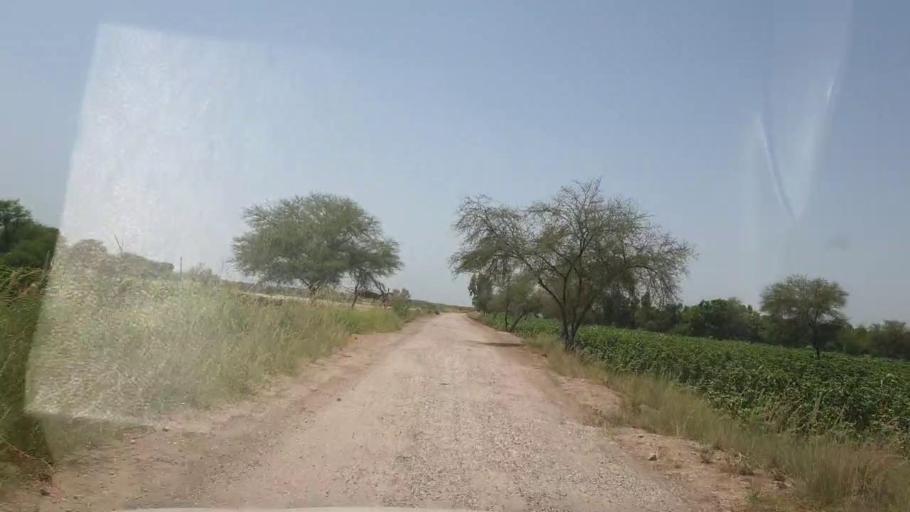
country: PK
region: Sindh
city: Bozdar
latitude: 27.1315
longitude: 68.6226
